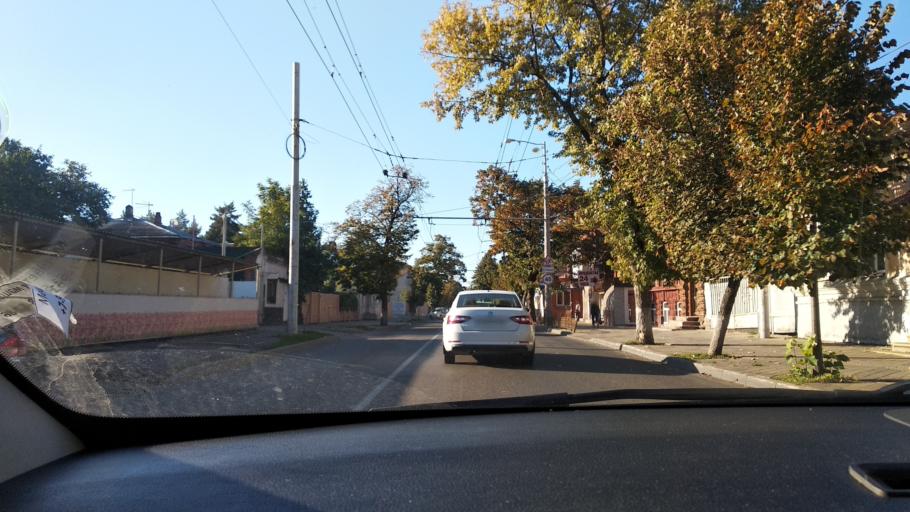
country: RU
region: Krasnodarskiy
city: Krasnodar
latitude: 45.0192
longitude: 38.9755
